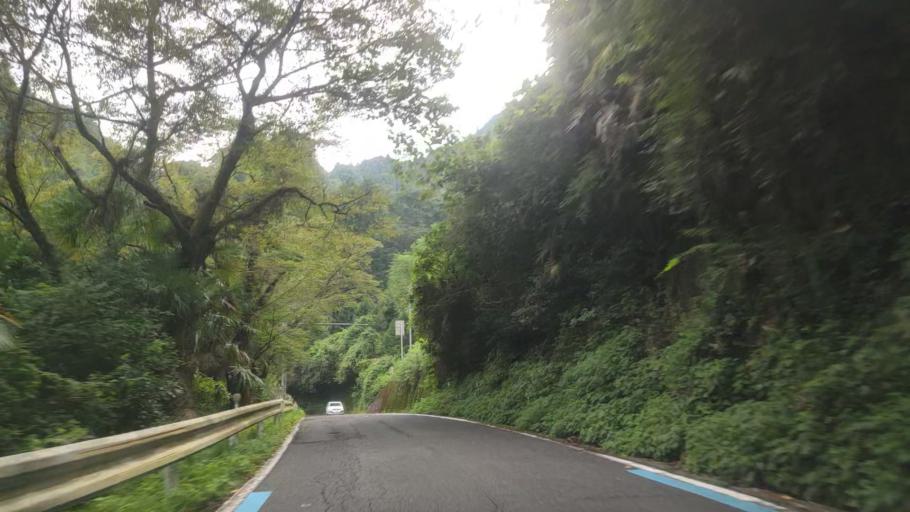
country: JP
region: Wakayama
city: Koya
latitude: 34.2462
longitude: 135.5460
